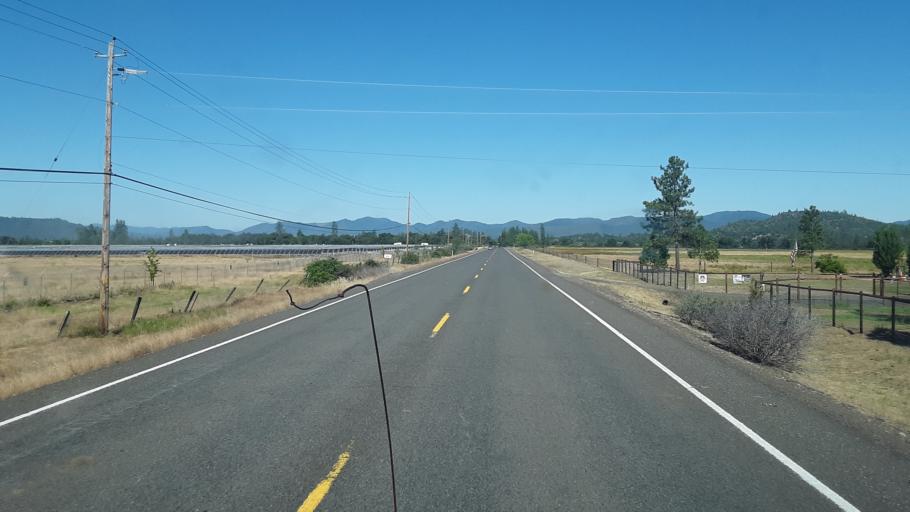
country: US
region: Oregon
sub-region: Jackson County
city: Eagle Point
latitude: 42.5237
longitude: -122.8253
